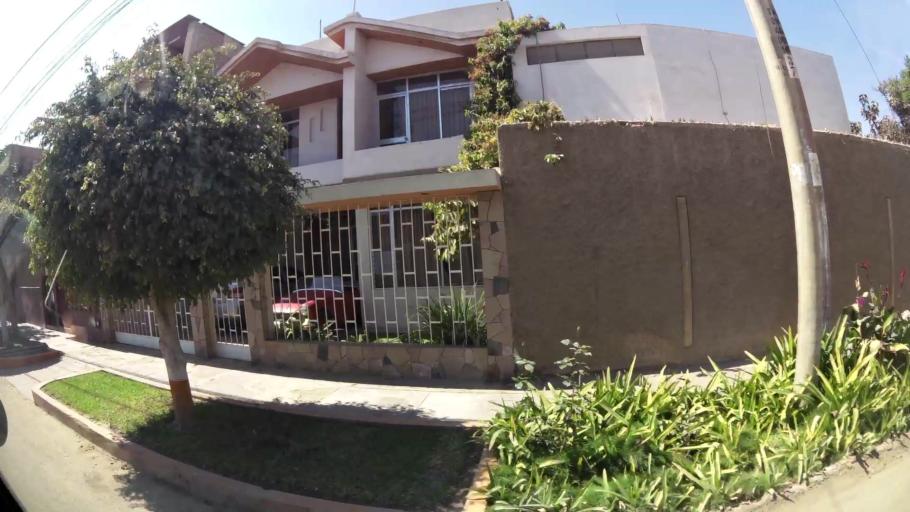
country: PE
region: Ica
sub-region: Provincia de Ica
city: Ica
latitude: -14.0728
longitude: -75.7316
